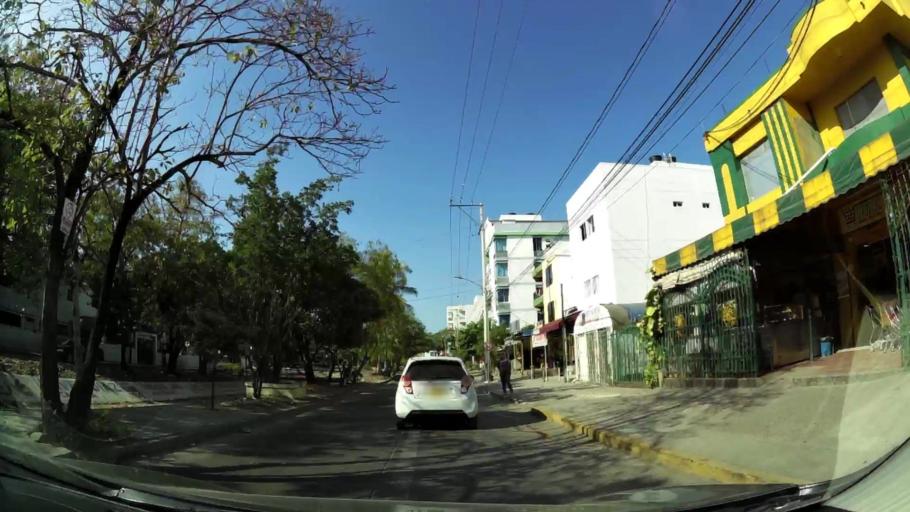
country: CO
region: Bolivar
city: Cartagena
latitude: 10.3877
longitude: -75.4856
